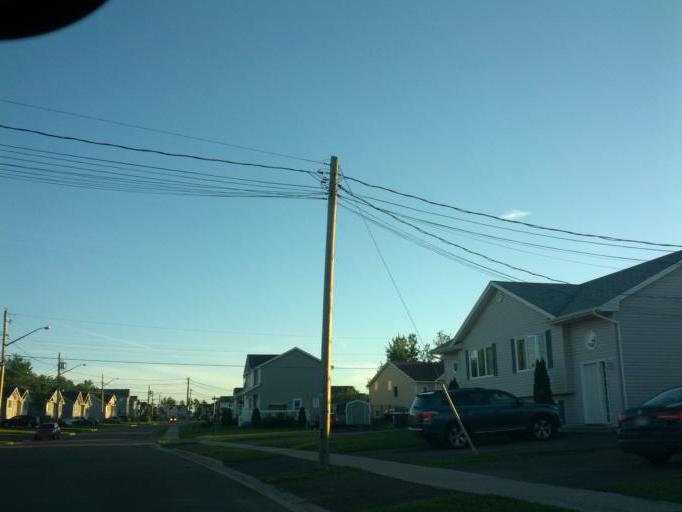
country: CA
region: New Brunswick
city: Moncton
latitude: 46.1178
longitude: -64.8517
